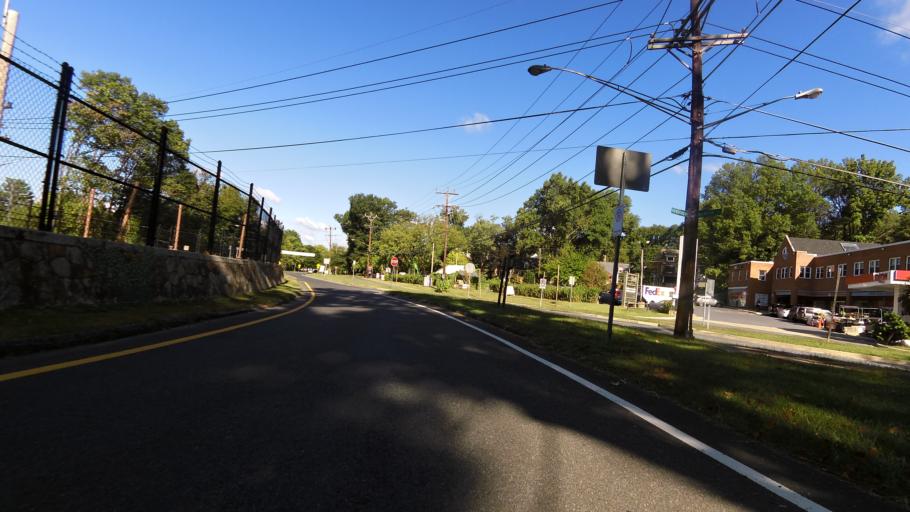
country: US
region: Maryland
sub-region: Montgomery County
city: Cabin John
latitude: 38.9686
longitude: -77.1386
